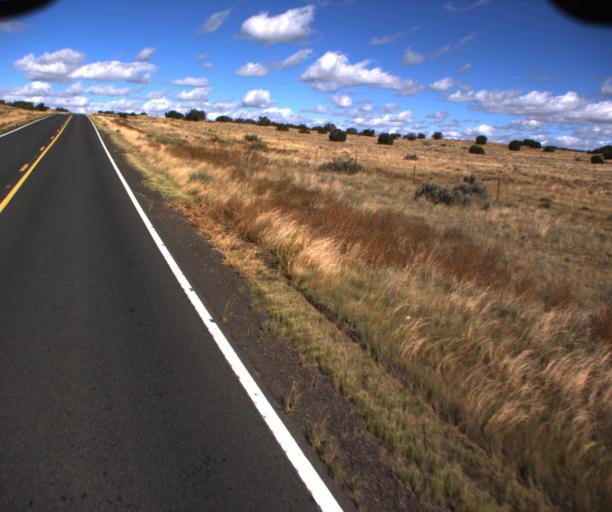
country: US
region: Arizona
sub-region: Apache County
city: Houck
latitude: 35.0161
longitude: -109.2379
